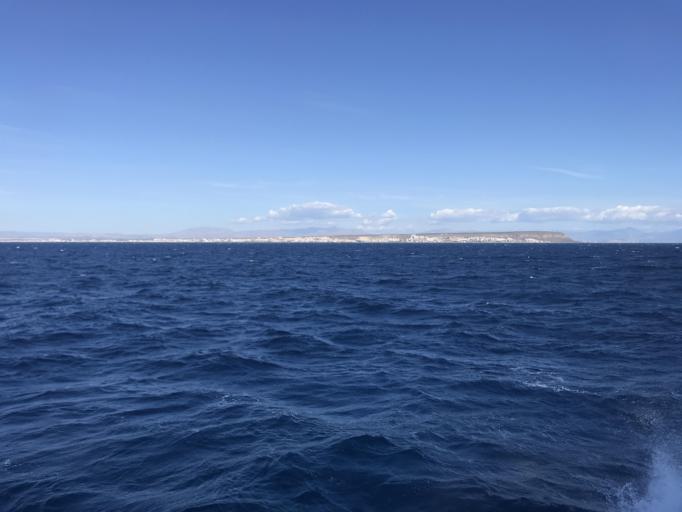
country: ES
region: Valencia
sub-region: Provincia de Alicante
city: Santa Pola
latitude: 38.1394
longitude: -0.5264
